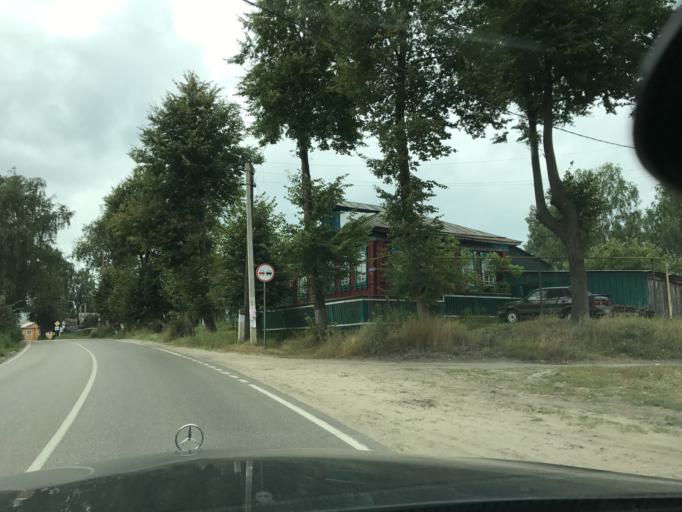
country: RU
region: Nizjnij Novgorod
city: Taremskoye
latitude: 55.9955
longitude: 43.0181
